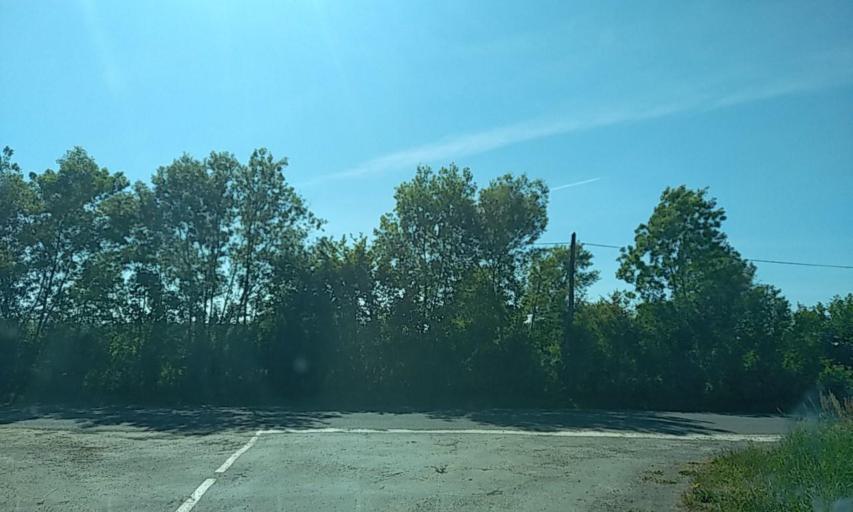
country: FR
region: Poitou-Charentes
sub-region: Departement des Deux-Sevres
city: Boisme
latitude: 46.7919
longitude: -0.4514
